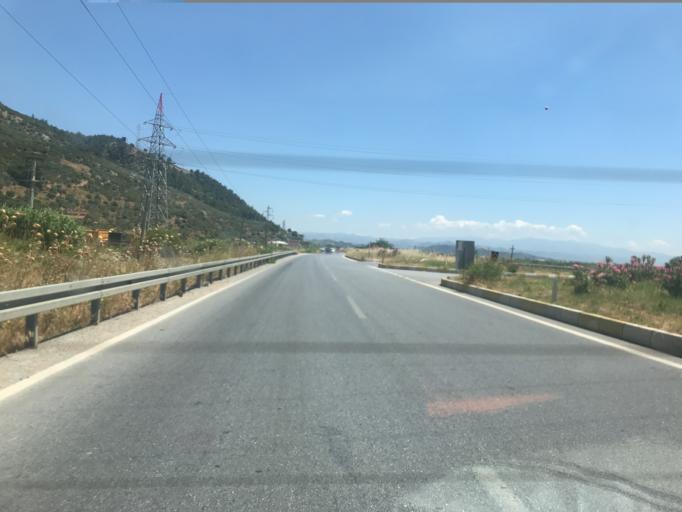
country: TR
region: Aydin
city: Soeke
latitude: 37.7989
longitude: 27.4709
